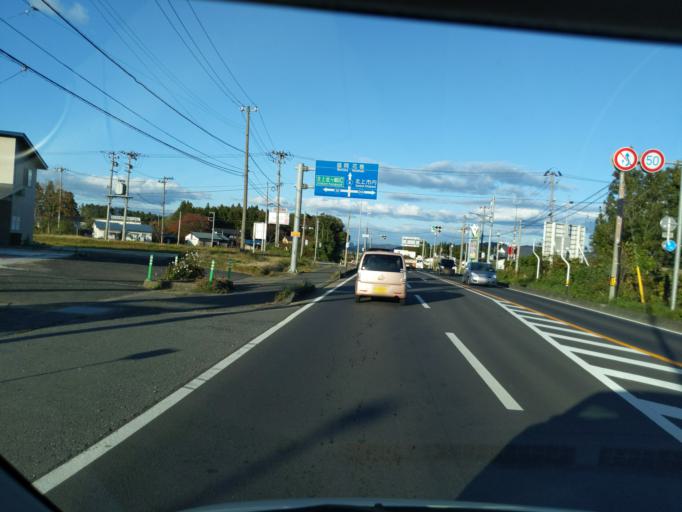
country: JP
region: Iwate
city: Kitakami
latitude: 39.2355
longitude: 141.0942
